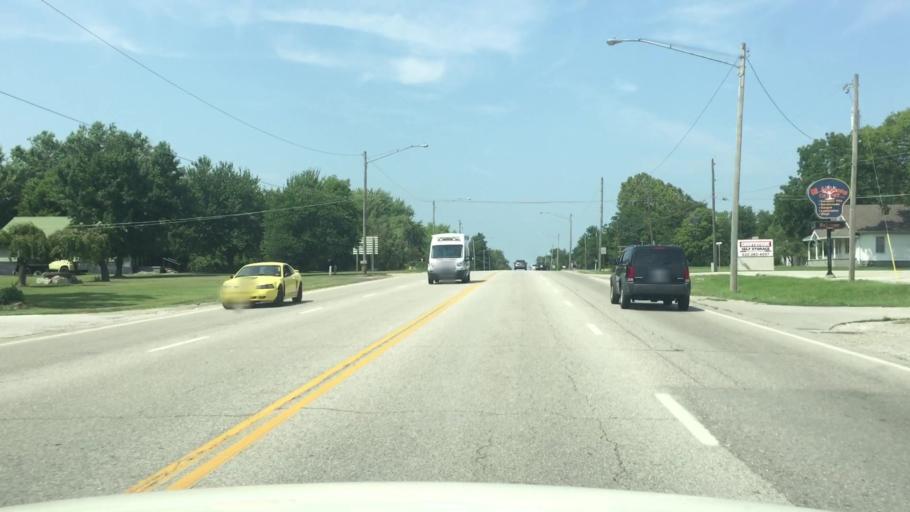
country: US
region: Kansas
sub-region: Crawford County
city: Frontenac
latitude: 37.4447
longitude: -94.7050
